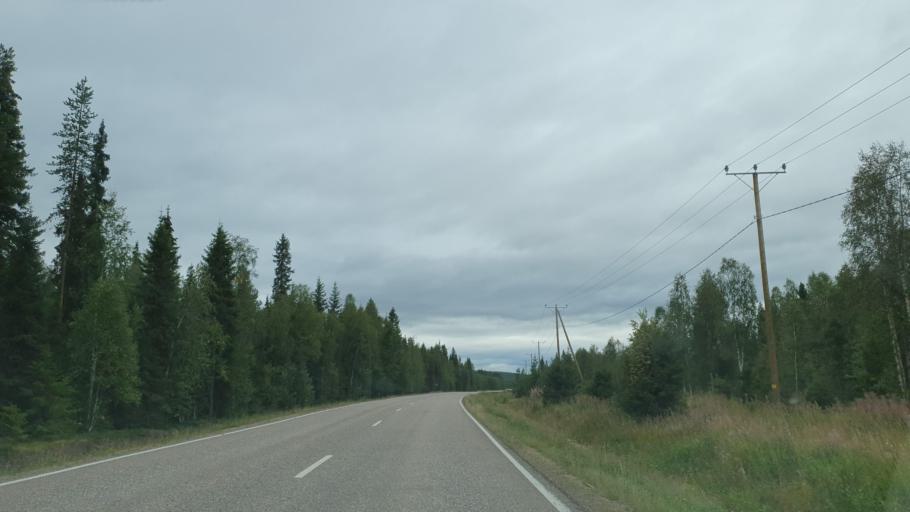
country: FI
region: Lapland
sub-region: Rovaniemi
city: Rovaniemi
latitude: 66.8341
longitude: 25.4109
